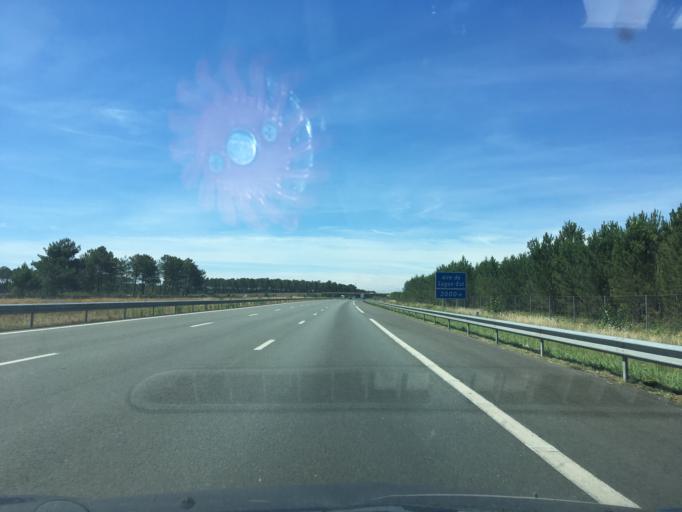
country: FR
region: Aquitaine
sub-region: Departement de la Gironde
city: Belin-Beliet
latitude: 44.4807
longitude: -0.8312
